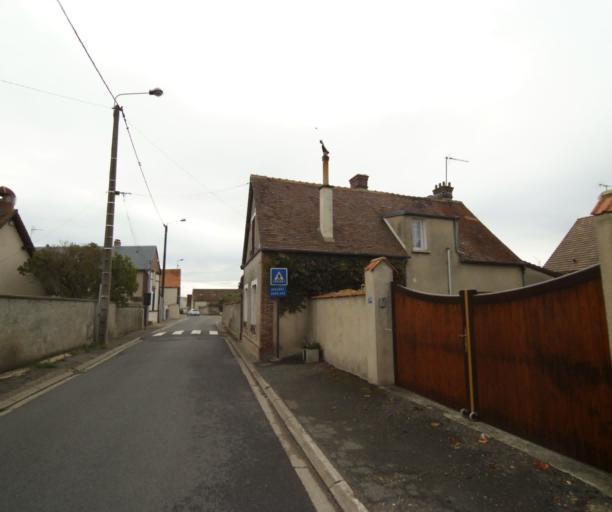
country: FR
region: Centre
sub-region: Departement d'Eure-et-Loir
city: Dreux
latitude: 48.7557
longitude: 1.3360
